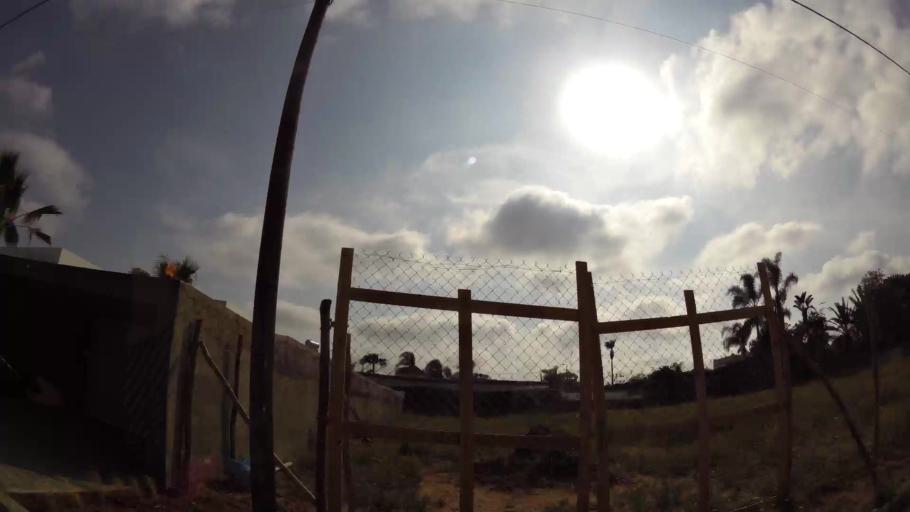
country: MA
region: Rabat-Sale-Zemmour-Zaer
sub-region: Rabat
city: Rabat
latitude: 33.9655
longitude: -6.8424
